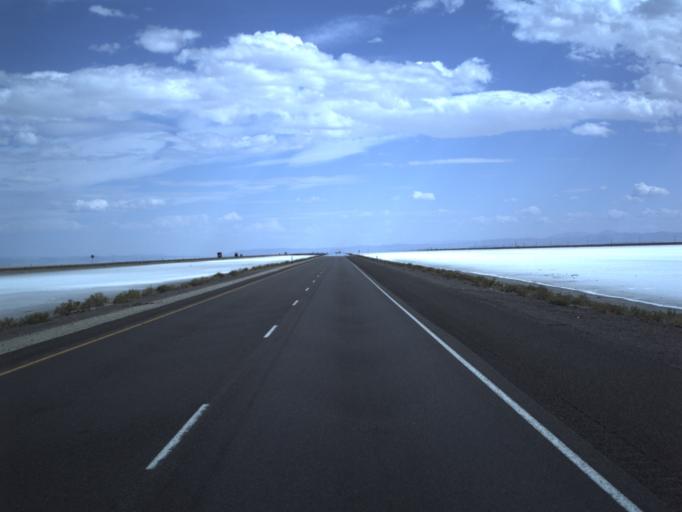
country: US
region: Utah
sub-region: Tooele County
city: Wendover
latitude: 40.7355
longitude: -113.7084
